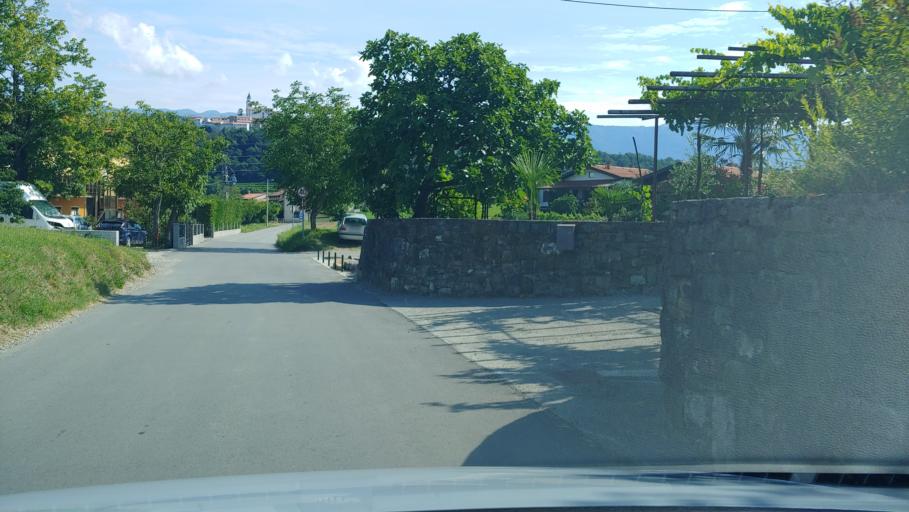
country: SI
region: Ajdovscina
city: Lokavec
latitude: 45.8752
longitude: 13.8556
